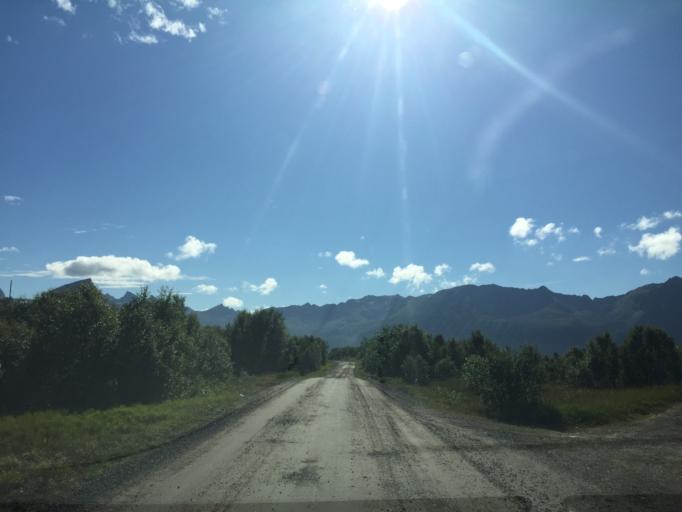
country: NO
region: Nordland
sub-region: Vagan
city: Kabelvag
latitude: 68.3565
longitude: 14.4500
